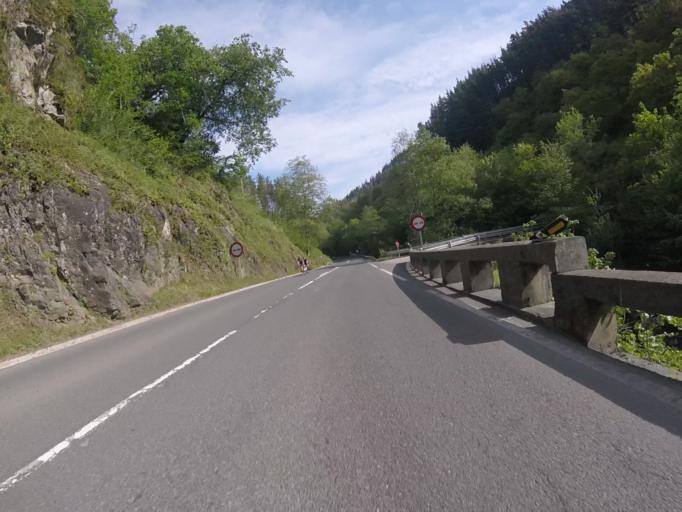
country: ES
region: Basque Country
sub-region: Provincia de Guipuzcoa
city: Anzuola
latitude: 43.1264
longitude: -2.3503
